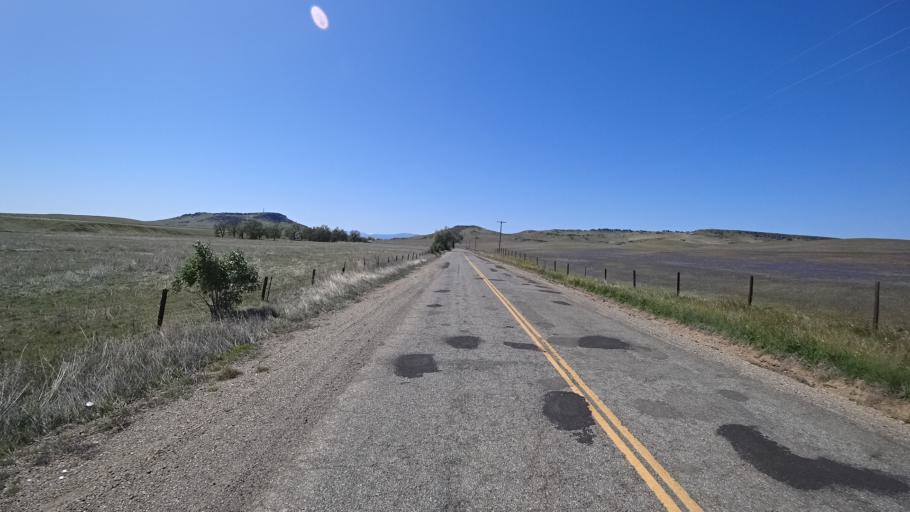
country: US
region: California
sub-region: Glenn County
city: Orland
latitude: 39.7760
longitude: -122.3170
